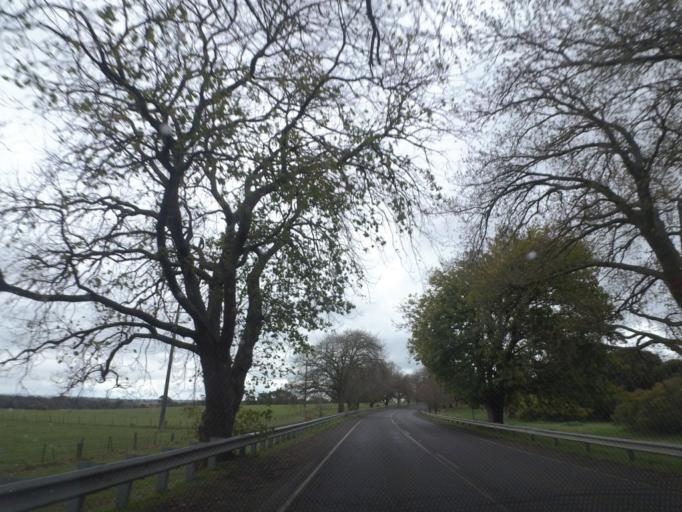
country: AU
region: Victoria
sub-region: Hume
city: Sunbury
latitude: -37.3387
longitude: 144.5264
